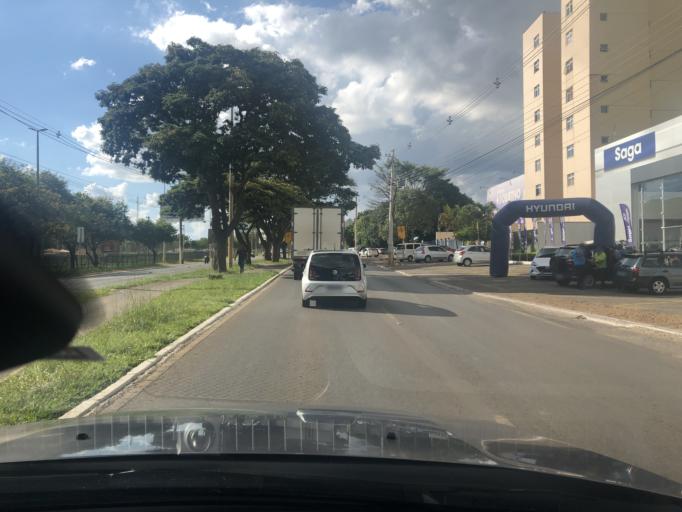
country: BR
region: Goias
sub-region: Luziania
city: Luziania
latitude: -16.0124
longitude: -48.0599
